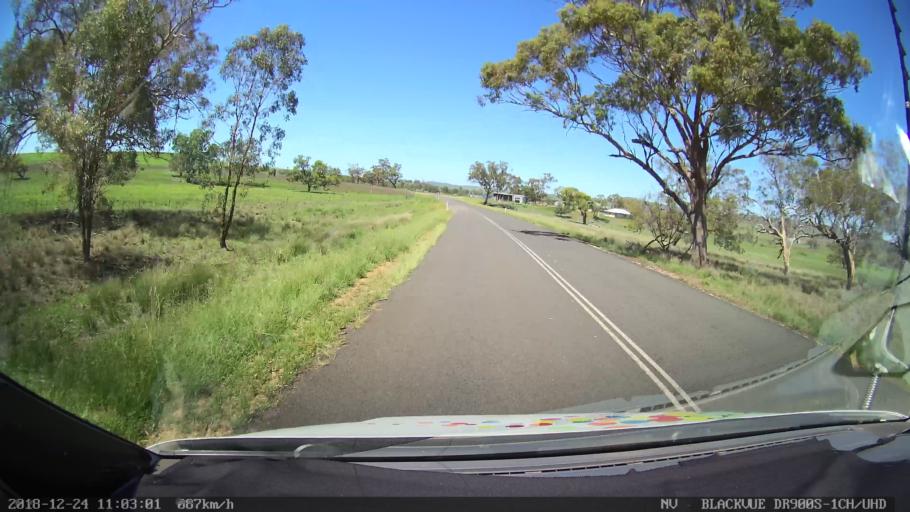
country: AU
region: New South Wales
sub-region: Upper Hunter Shire
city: Merriwa
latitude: -32.0914
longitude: 150.3703
